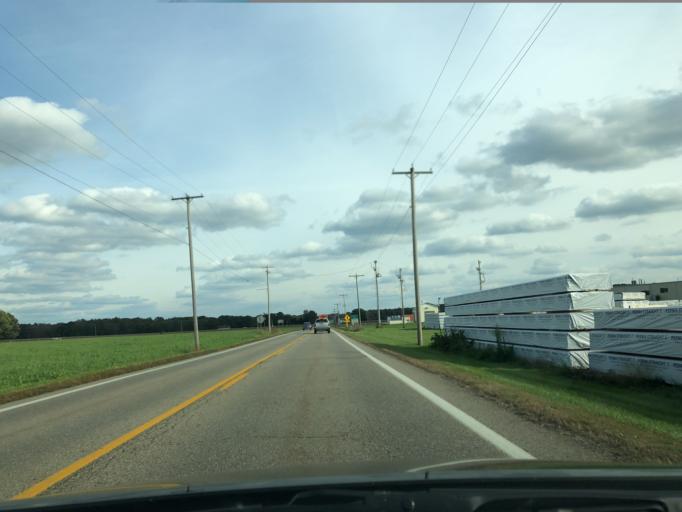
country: US
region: Ohio
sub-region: Stark County
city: Beach City
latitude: 40.6428
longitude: -81.5830
